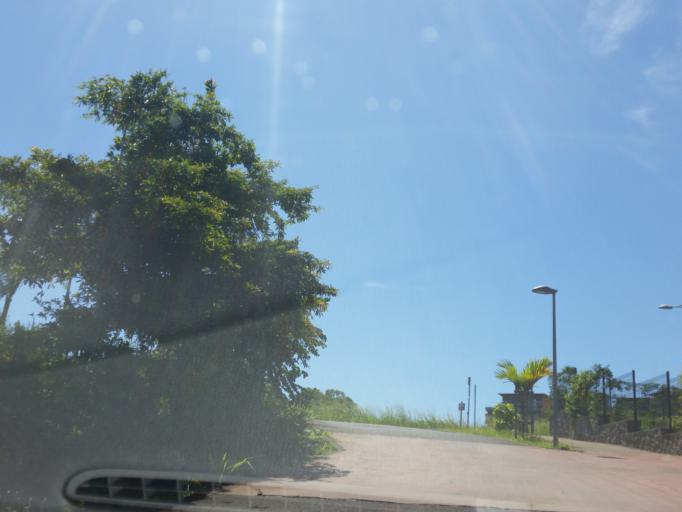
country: RE
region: Reunion
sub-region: Reunion
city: Sainte-Marie
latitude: -20.9168
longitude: 55.5239
